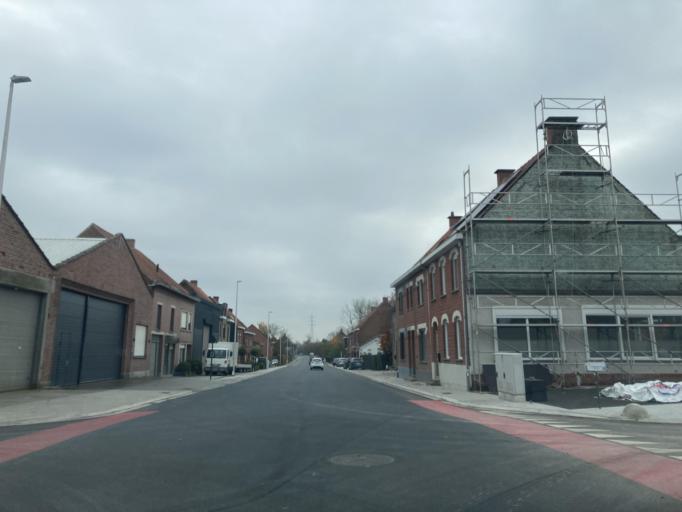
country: BE
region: Flanders
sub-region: Provincie West-Vlaanderen
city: Lendelede
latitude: 50.8643
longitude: 3.1841
